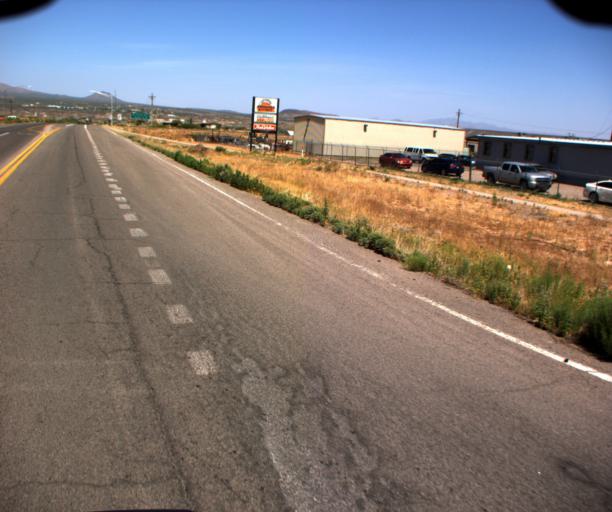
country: US
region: Arizona
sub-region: Gila County
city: Peridot
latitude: 33.2928
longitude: -110.4357
